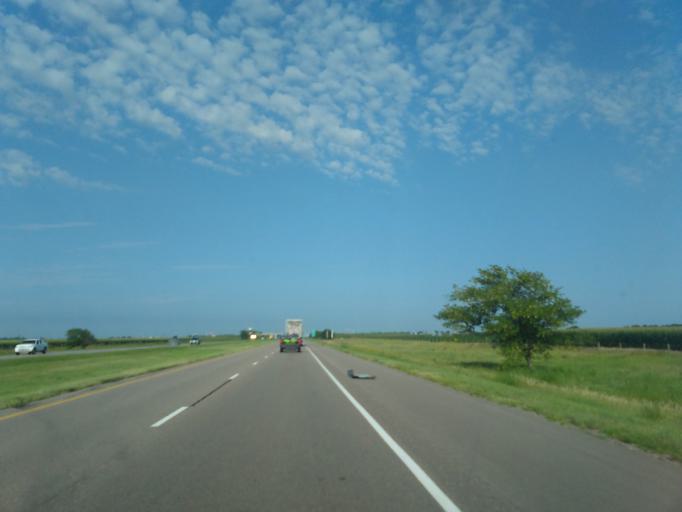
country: US
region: Nebraska
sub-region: York County
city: York
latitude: 40.8212
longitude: -97.6277
